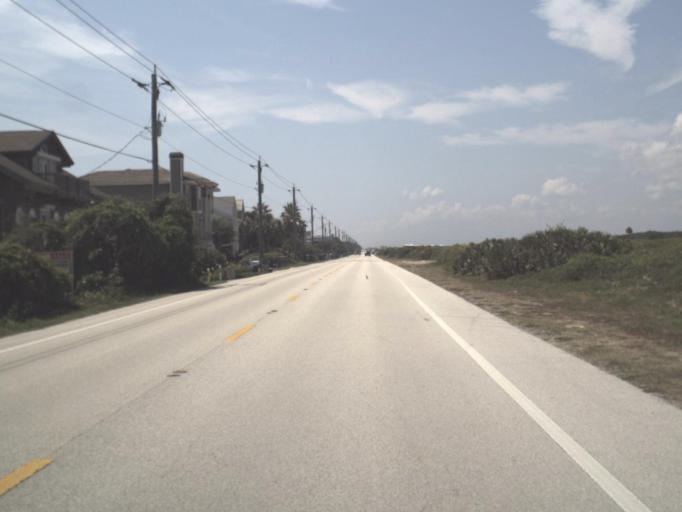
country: US
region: Florida
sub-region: Saint Johns County
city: Villano Beach
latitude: 30.0119
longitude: -81.3206
